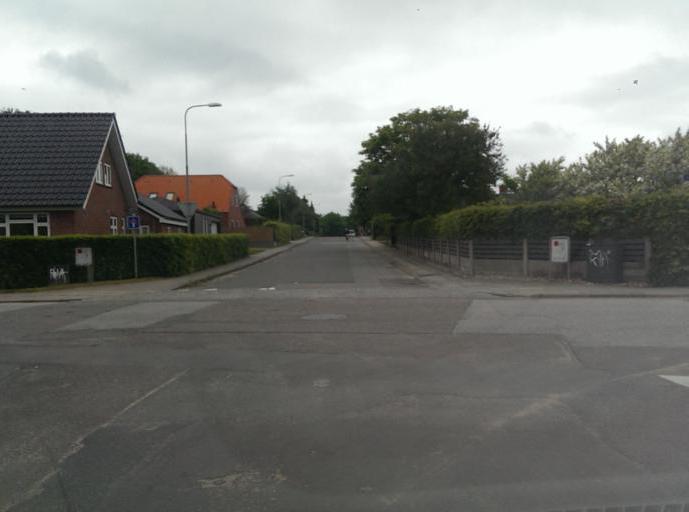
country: DK
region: South Denmark
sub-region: Fano Kommune
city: Nordby
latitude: 55.5209
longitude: 8.3641
